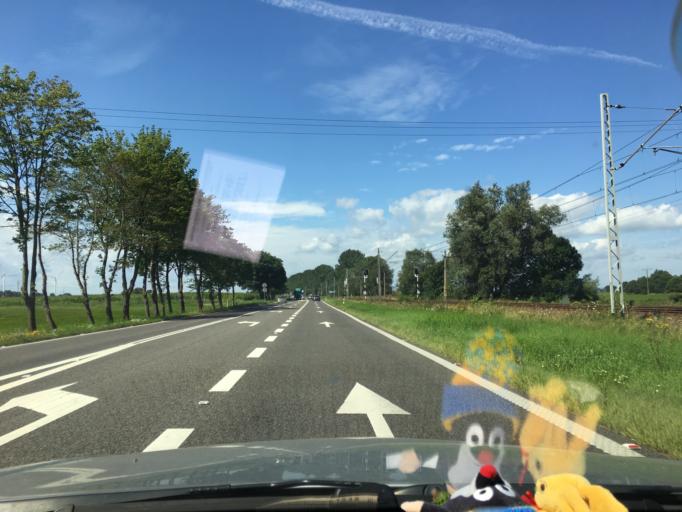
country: PL
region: West Pomeranian Voivodeship
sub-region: Powiat kamienski
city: Wolin
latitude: 53.8468
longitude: 14.6846
